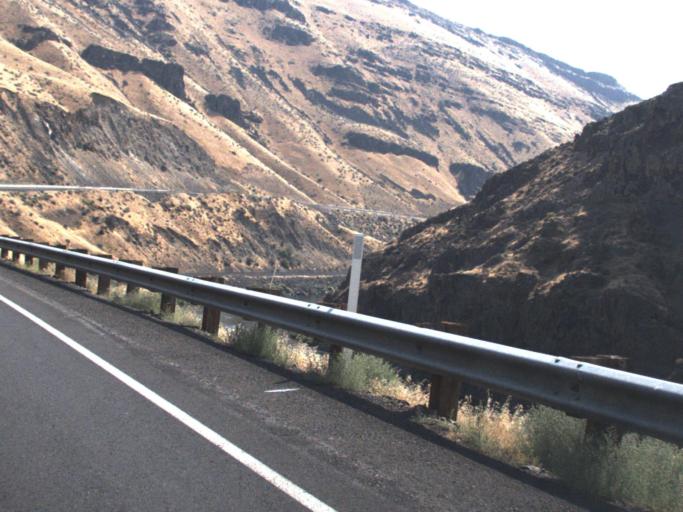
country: US
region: Washington
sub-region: Yakima County
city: Selah
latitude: 46.7289
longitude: -120.4522
